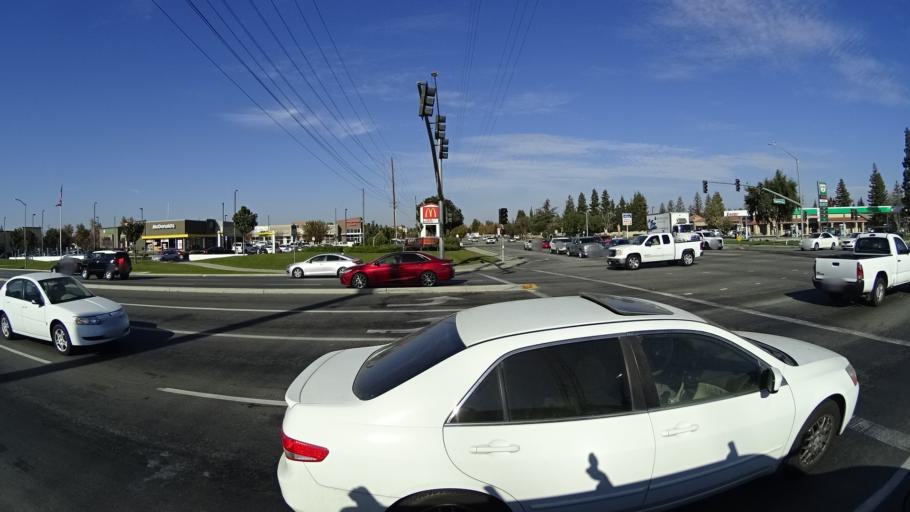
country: US
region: California
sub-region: Kern County
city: Greenacres
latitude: 35.4014
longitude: -119.0926
